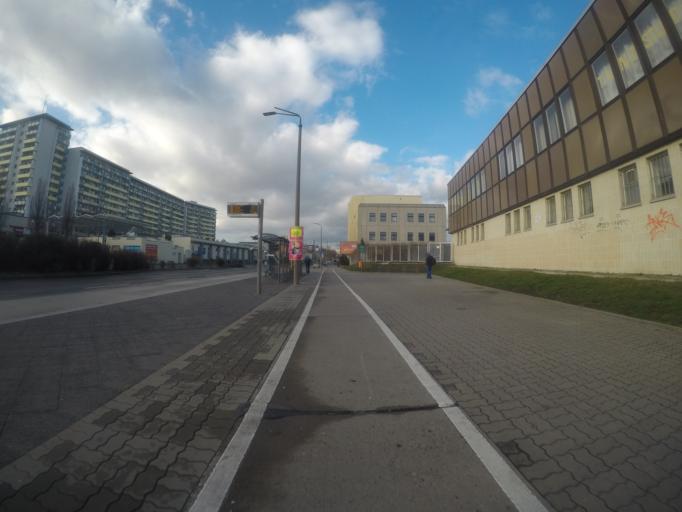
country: DE
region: Berlin
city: Kaulsdorf
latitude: 52.5213
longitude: 13.5880
